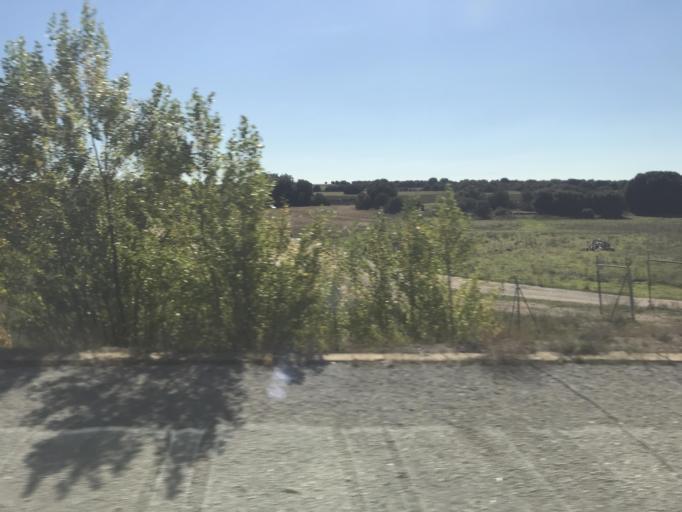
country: ES
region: Castille-La Mancha
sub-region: Provincia de Guadalajara
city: Alaminos
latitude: 40.9001
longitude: -2.6962
